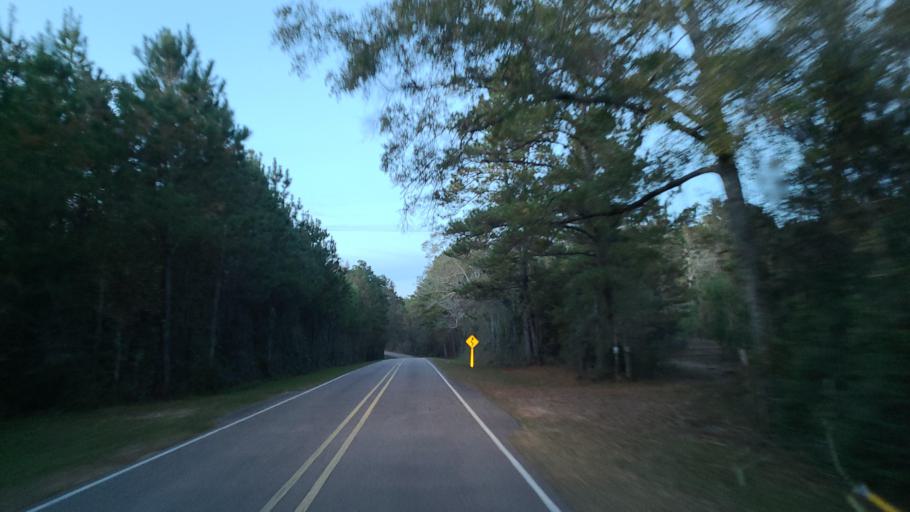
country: US
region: Mississippi
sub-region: Perry County
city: New Augusta
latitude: 31.1410
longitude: -89.2016
